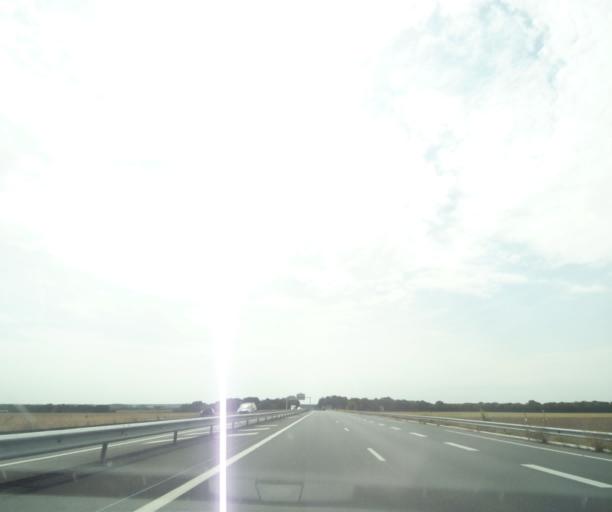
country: FR
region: Poitou-Charentes
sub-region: Departement des Deux-Sevres
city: Fors
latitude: 46.2358
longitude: -0.4377
